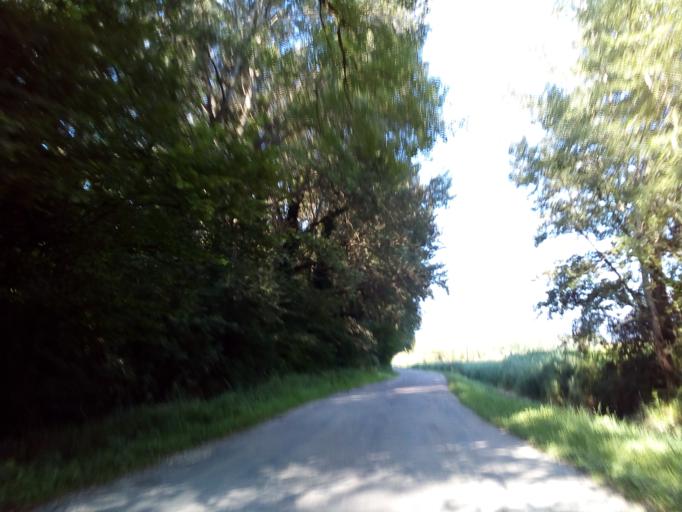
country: FR
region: Rhone-Alpes
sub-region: Departement de l'Isere
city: Saint-Nazaire-les-Eymes
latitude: 45.2428
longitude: 5.8609
